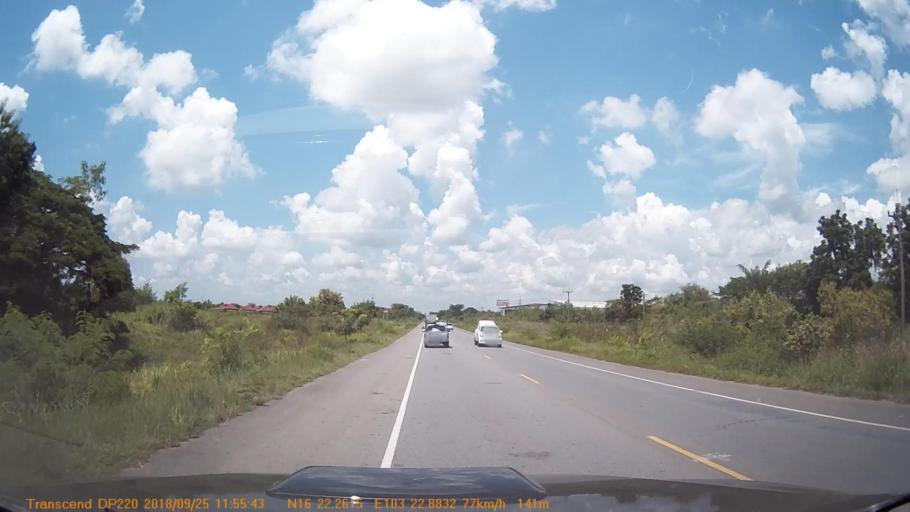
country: TH
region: Kalasin
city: Yang Talat
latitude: 16.3712
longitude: 103.3812
